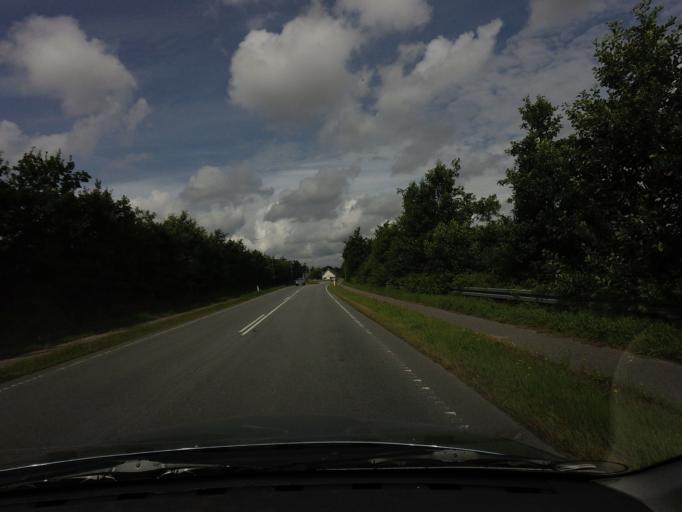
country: DK
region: North Denmark
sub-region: Hjorring Kommune
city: Tars
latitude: 57.3627
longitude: 10.1978
